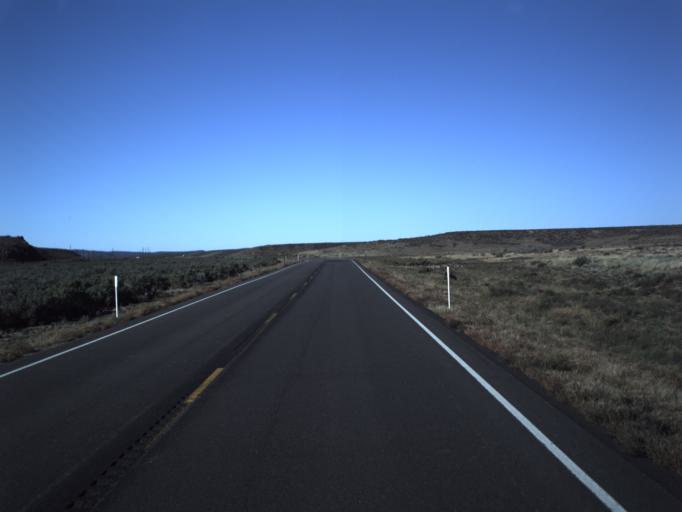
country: US
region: Utah
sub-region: Washington County
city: Enterprise
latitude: 37.7859
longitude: -113.9591
